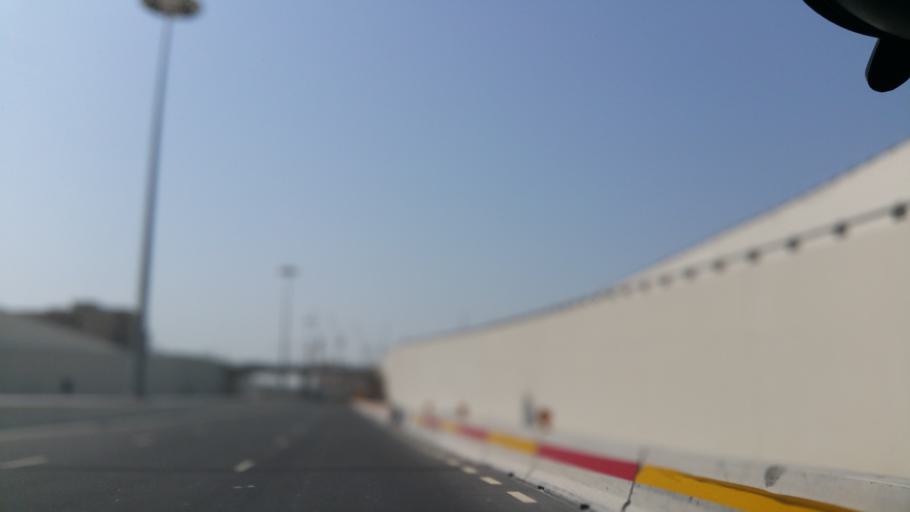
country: QA
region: Baladiyat Umm Salal
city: Umm Salal Muhammad
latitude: 25.4101
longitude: 51.5107
